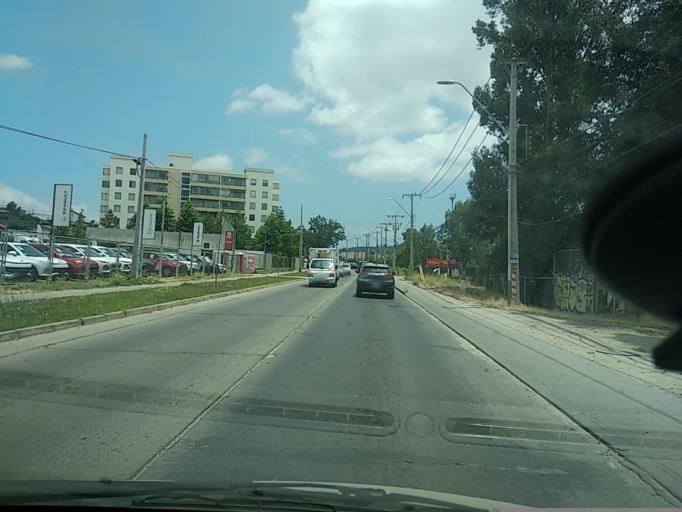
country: CL
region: Valparaiso
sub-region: Provincia de Marga Marga
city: Quilpue
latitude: -33.0426
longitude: -71.4243
